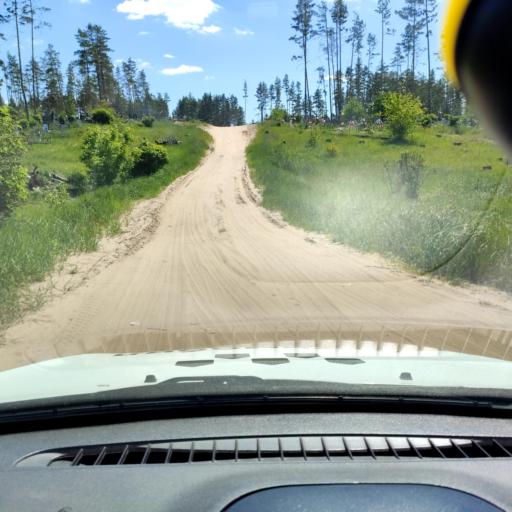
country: RU
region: Samara
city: Zhigulevsk
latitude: 53.5354
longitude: 49.5518
